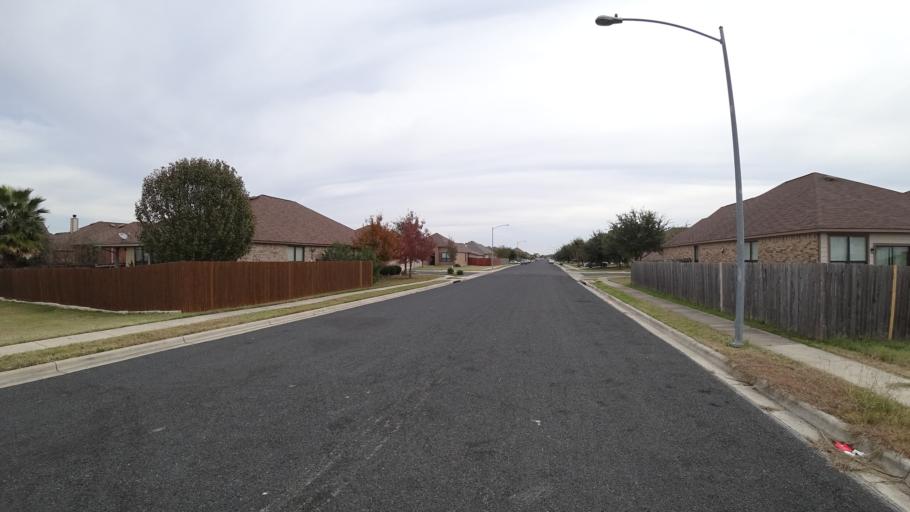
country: US
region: Texas
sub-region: Travis County
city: Onion Creek
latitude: 30.1522
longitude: -97.7495
